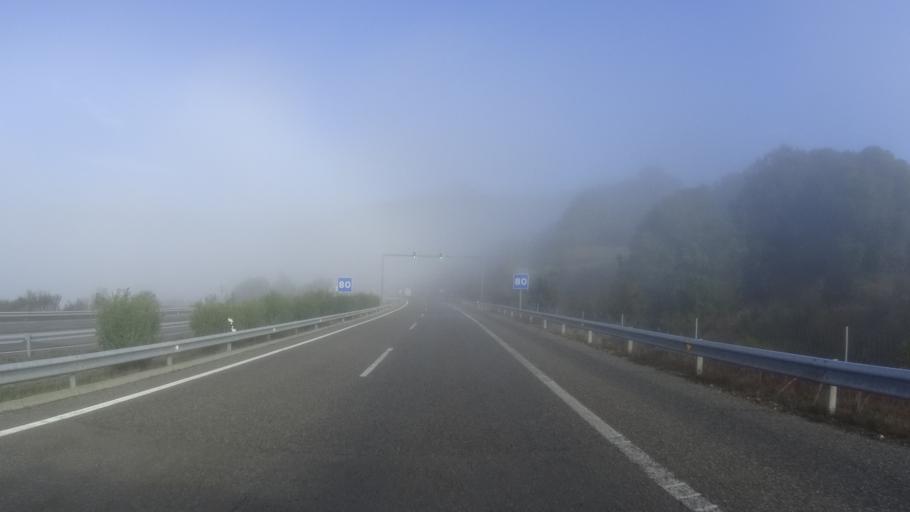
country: ES
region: Galicia
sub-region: Provincia de Lugo
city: San Roman
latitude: 42.7807
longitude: -7.1006
